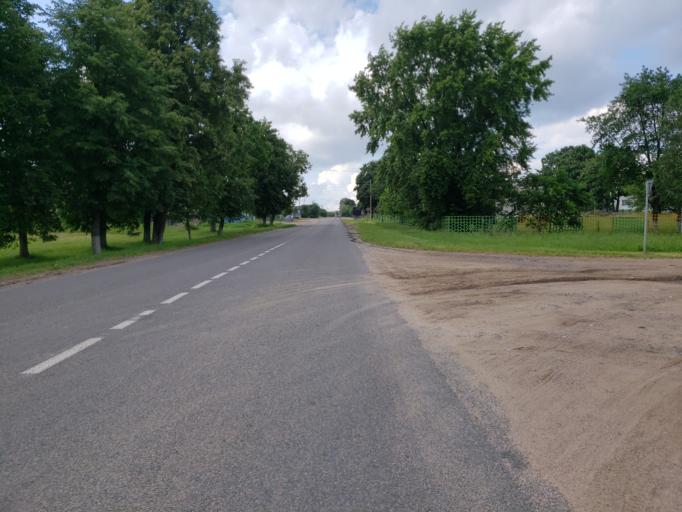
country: BY
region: Minsk
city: Chervyen'
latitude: 53.7333
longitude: 28.3882
